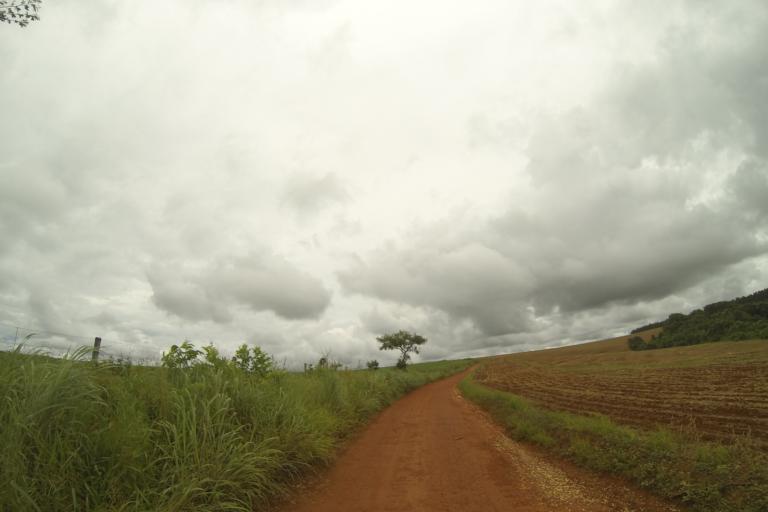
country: BR
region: Minas Gerais
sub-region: Ibia
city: Ibia
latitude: -19.7165
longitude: -46.5796
